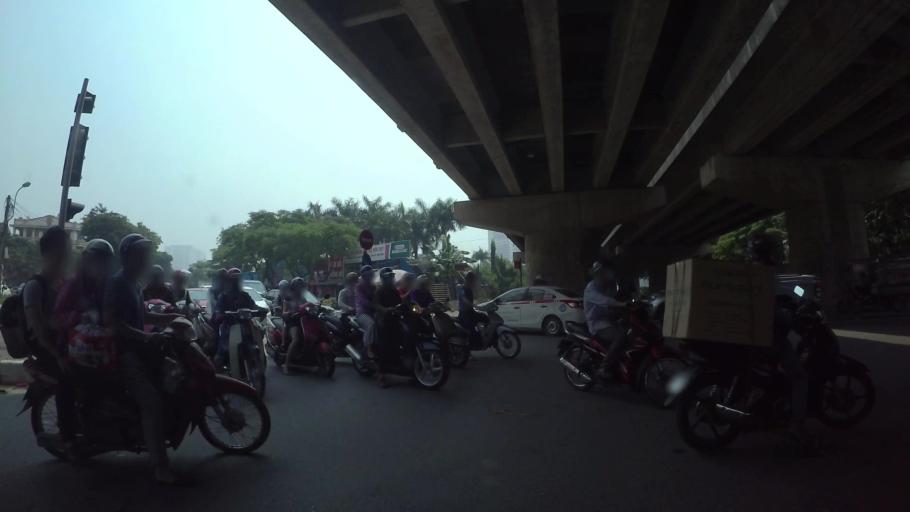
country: VN
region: Ha Noi
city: Van Dien
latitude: 20.9690
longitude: 105.8286
